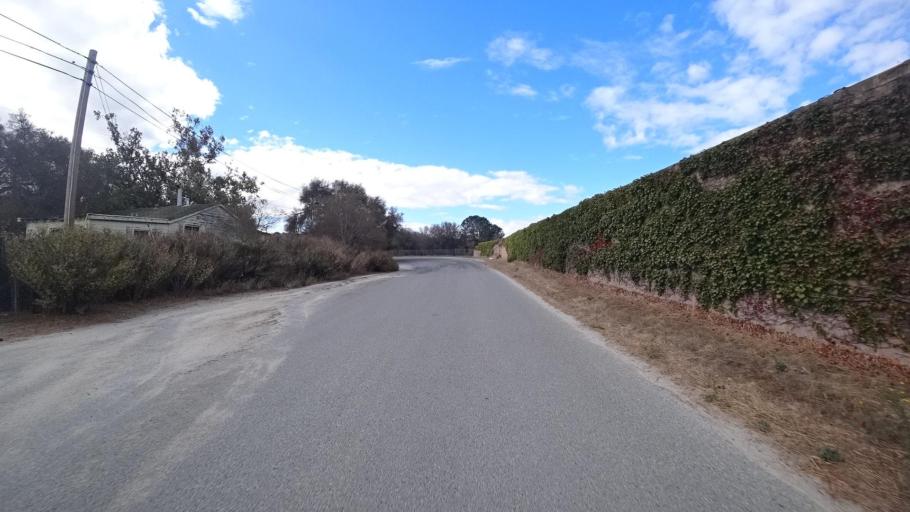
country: US
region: California
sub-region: Monterey County
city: Salinas
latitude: 36.6079
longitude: -121.6911
